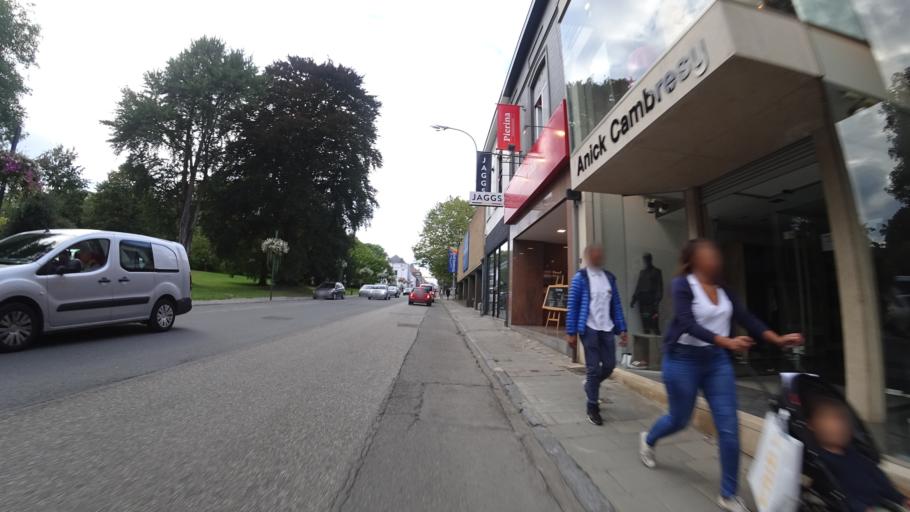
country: BE
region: Wallonia
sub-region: Province du Brabant Wallon
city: Waterloo
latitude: 50.7127
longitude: 4.4001
